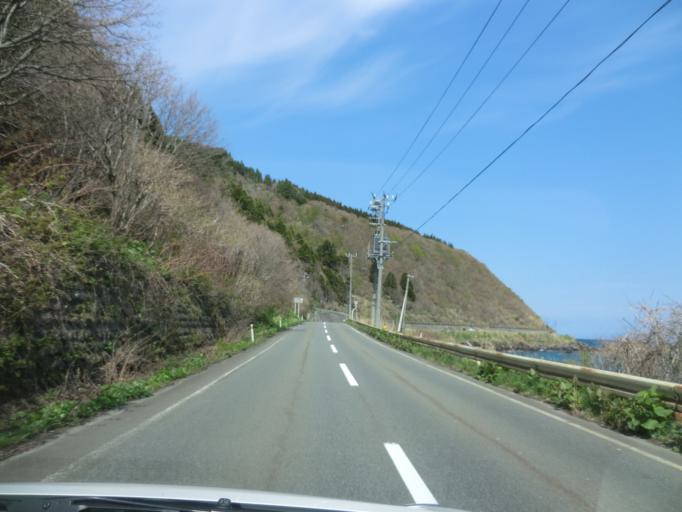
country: JP
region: Aomori
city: Mutsu
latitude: 41.4773
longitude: 141.0722
